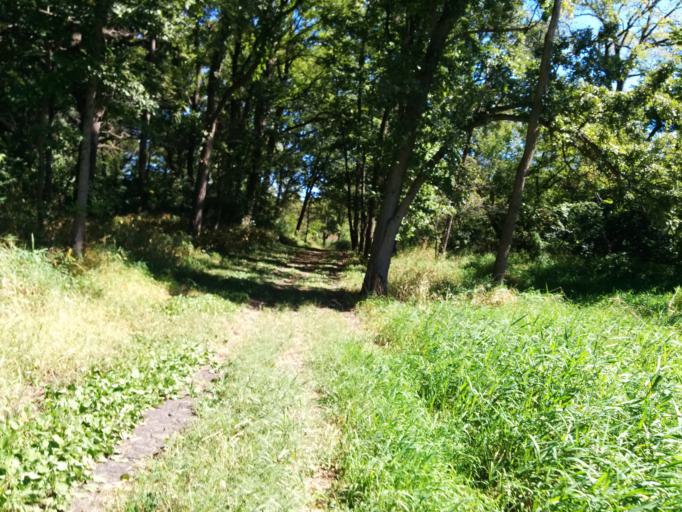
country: US
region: Illinois
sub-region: DuPage County
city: Oak Brook
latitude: 41.8246
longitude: -87.9126
